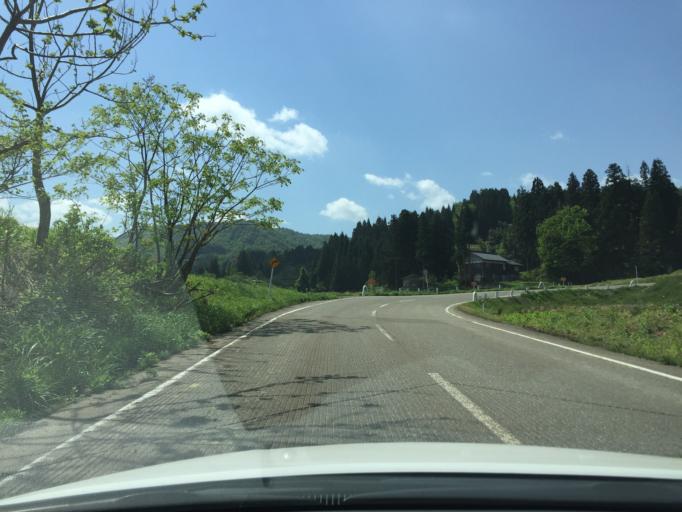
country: JP
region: Niigata
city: Tochio-honcho
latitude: 37.4747
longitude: 139.0486
